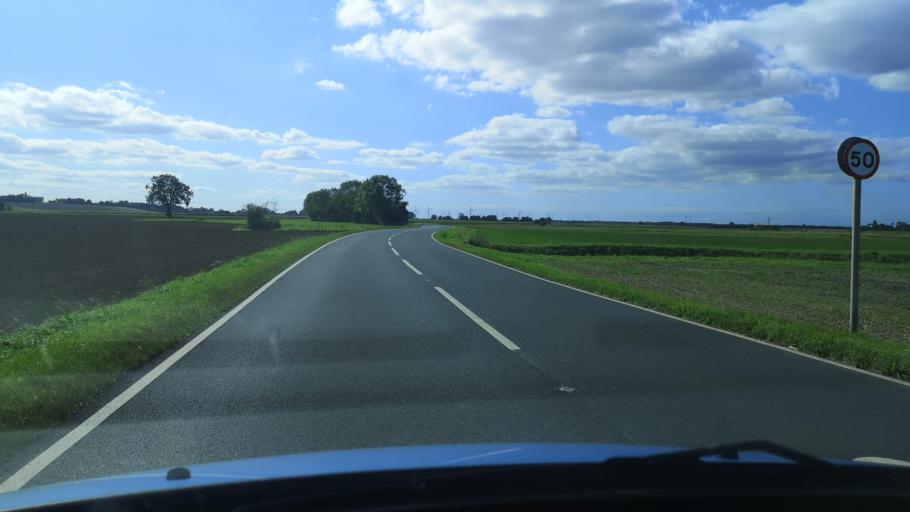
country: GB
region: England
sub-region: North Lincolnshire
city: Crowle
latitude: 53.6199
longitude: -0.8091
